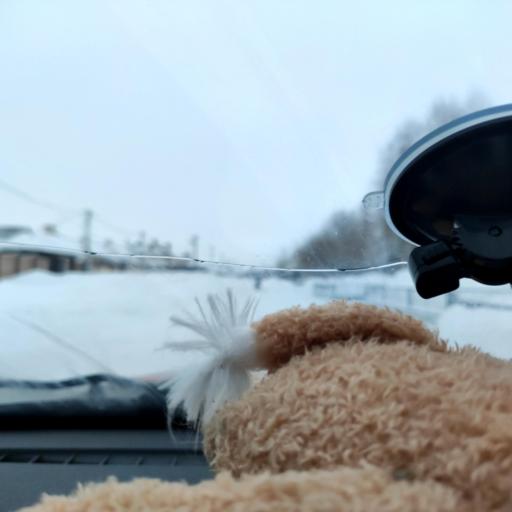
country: RU
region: Samara
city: Podstepki
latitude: 53.5096
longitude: 49.1758
